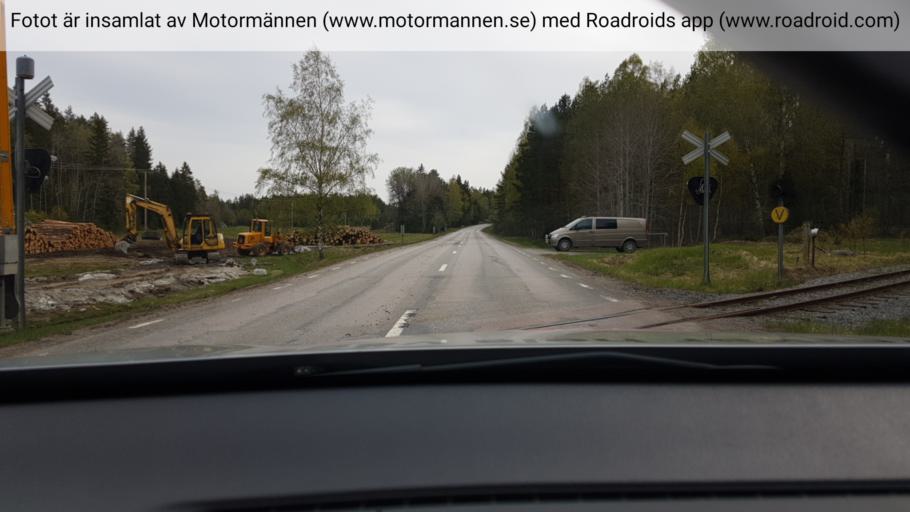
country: SE
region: Stockholm
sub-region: Norrtalje Kommun
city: Nykvarn
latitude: 59.9080
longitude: 18.0960
